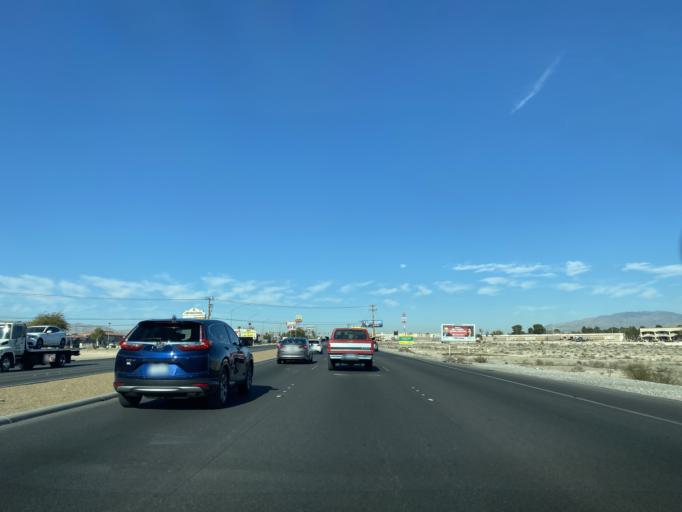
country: US
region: Nevada
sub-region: Clark County
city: Las Vegas
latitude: 36.2140
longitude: -115.2091
